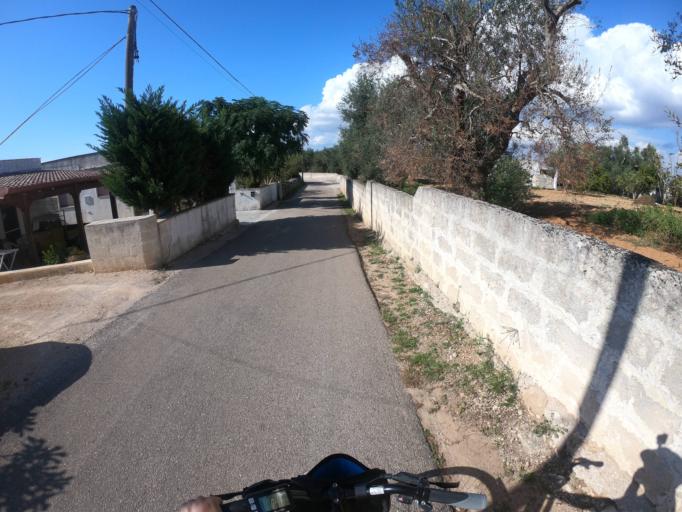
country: IT
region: Apulia
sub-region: Provincia di Lecce
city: Galatone
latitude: 40.1457
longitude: 18.0418
